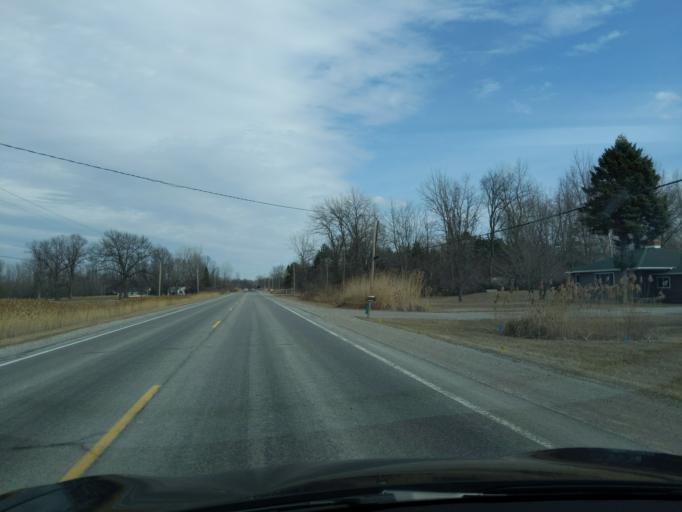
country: US
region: Michigan
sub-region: Bay County
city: Bay City
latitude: 43.6676
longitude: -83.9440
